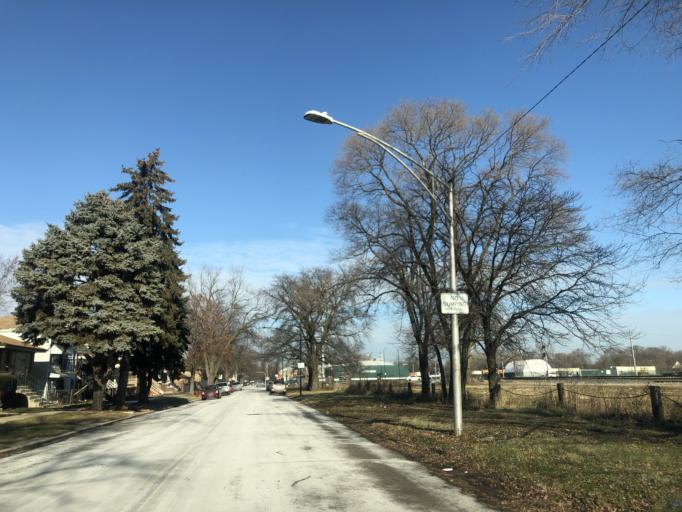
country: US
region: Illinois
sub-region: Cook County
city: Evergreen Park
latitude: 41.7632
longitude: -87.6794
